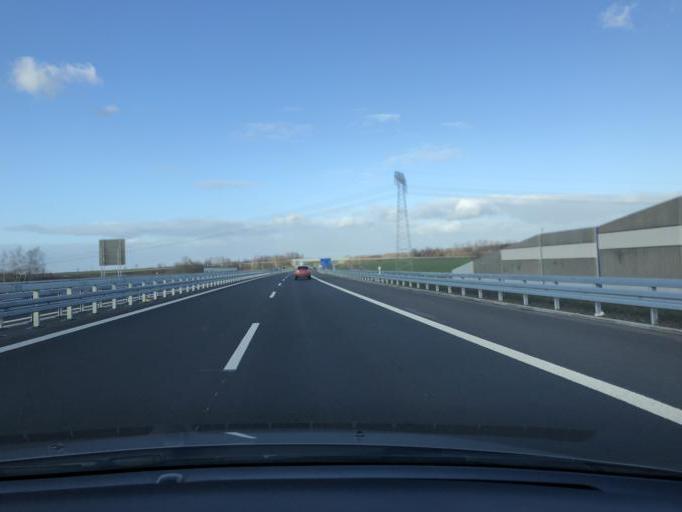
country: DE
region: Saxony
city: Borna
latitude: 51.1469
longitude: 12.5038
